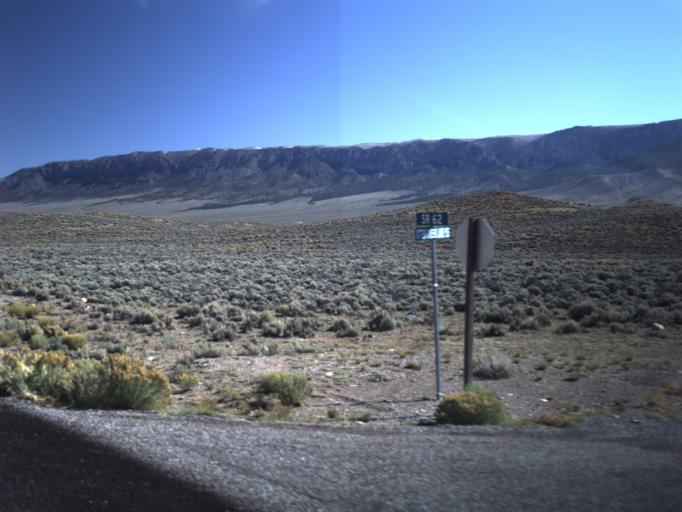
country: US
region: Utah
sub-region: Piute County
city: Junction
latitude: 38.2196
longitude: -112.0001
